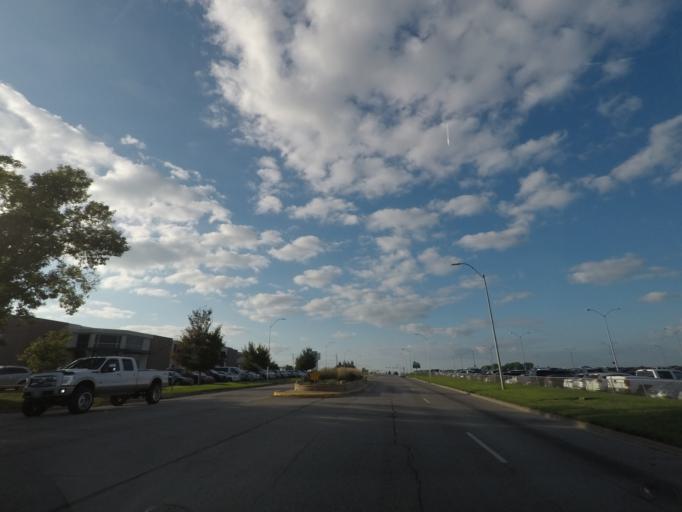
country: US
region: Iowa
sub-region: Warren County
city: Norwalk
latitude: 41.5302
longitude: -93.6451
